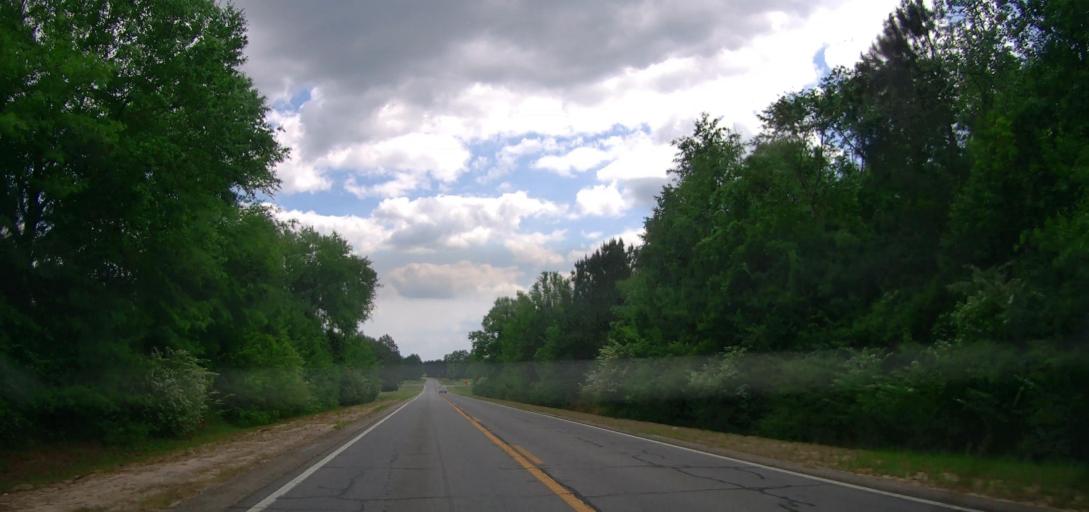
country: US
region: Georgia
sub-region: Laurens County
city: East Dublin
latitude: 32.5047
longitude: -82.8352
